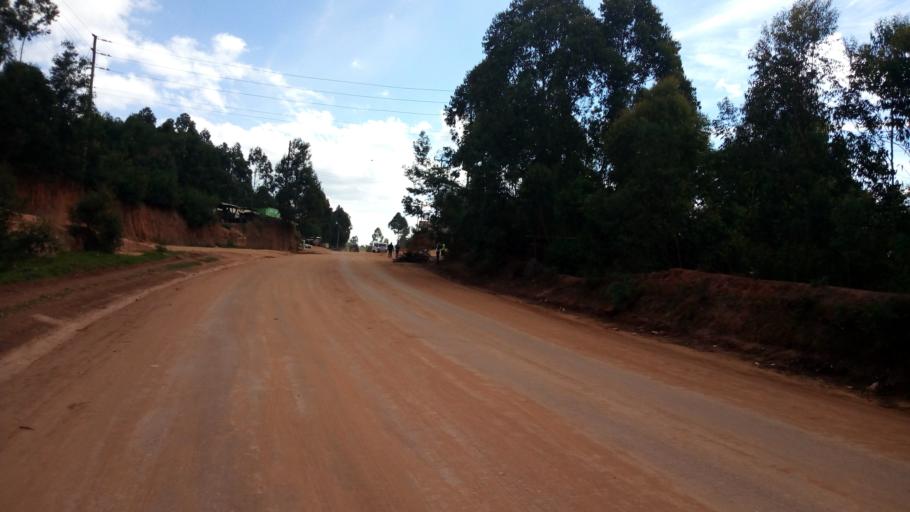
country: KE
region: Makueni
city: Wote
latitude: -1.6558
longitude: 37.4573
